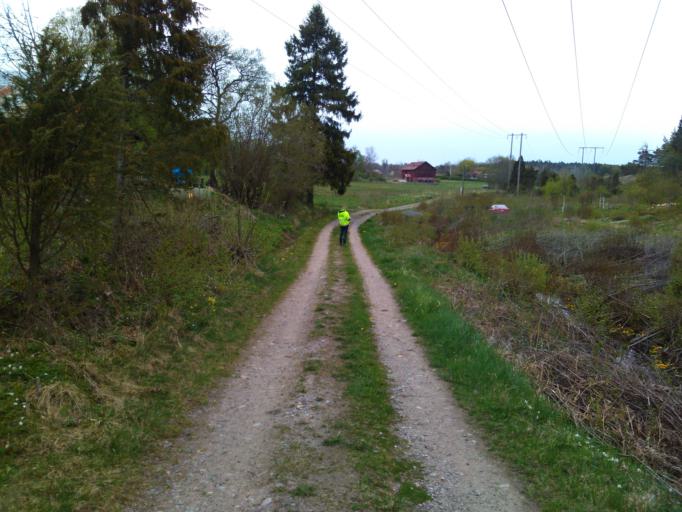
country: SE
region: Stockholm
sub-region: Norrtalje Kommun
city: Norrtalje
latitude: 59.6565
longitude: 18.6626
